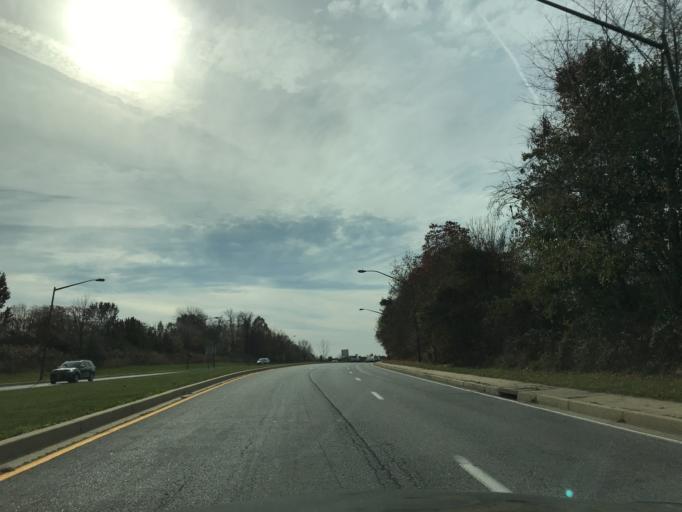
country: US
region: Maryland
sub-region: Howard County
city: Columbia
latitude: 39.1945
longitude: -76.8094
